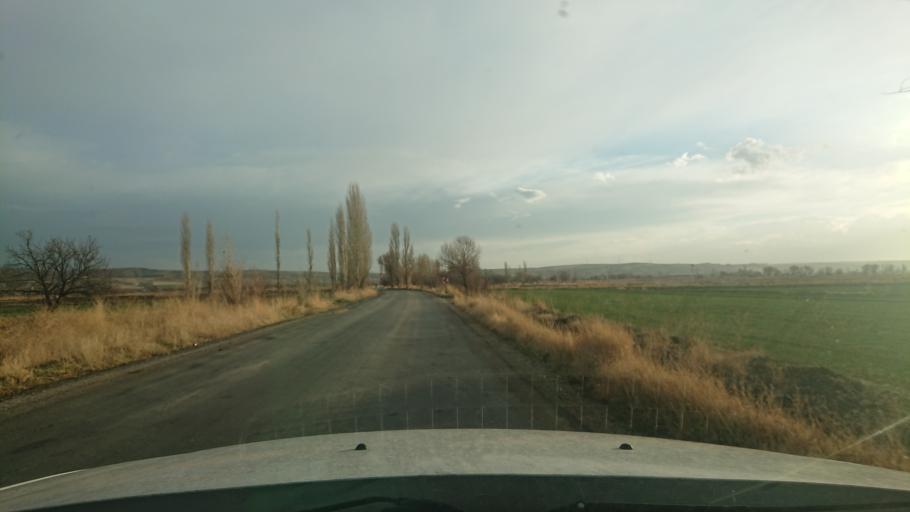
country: TR
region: Aksaray
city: Acipinar
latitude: 38.4766
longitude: 33.8757
